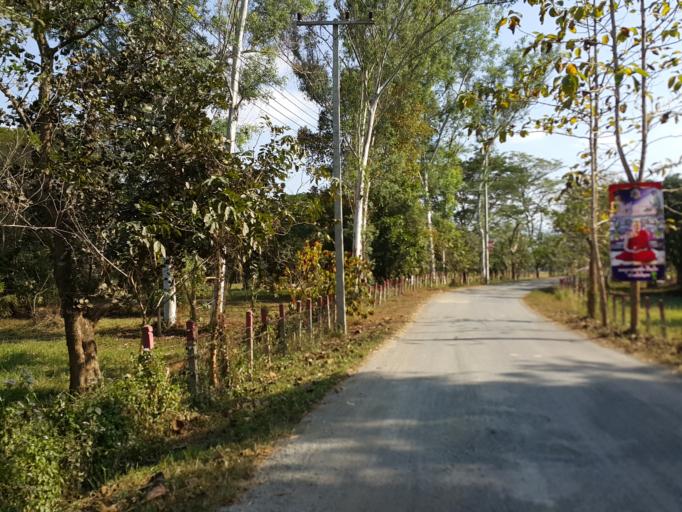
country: TH
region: Chiang Mai
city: Mae On
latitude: 18.8054
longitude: 99.2281
